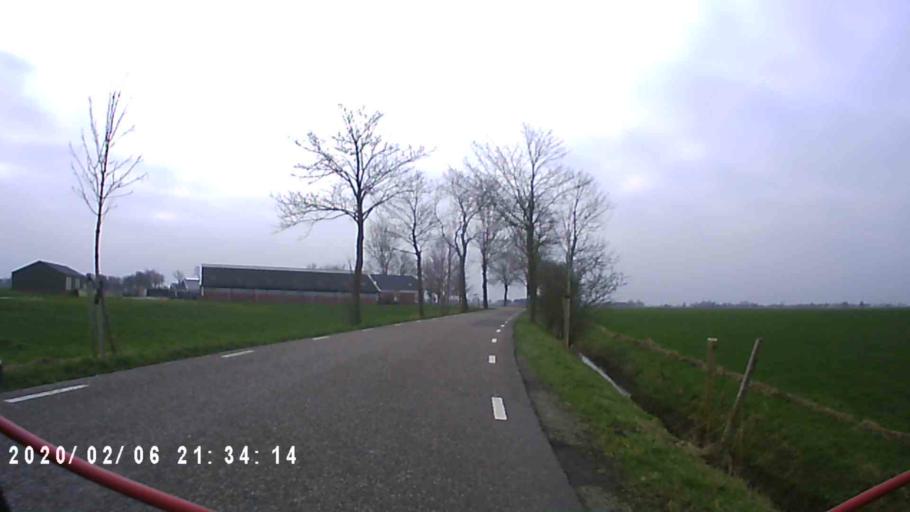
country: NL
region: Groningen
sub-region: Gemeente Zuidhorn
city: Noordhorn
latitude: 53.2740
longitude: 6.3907
